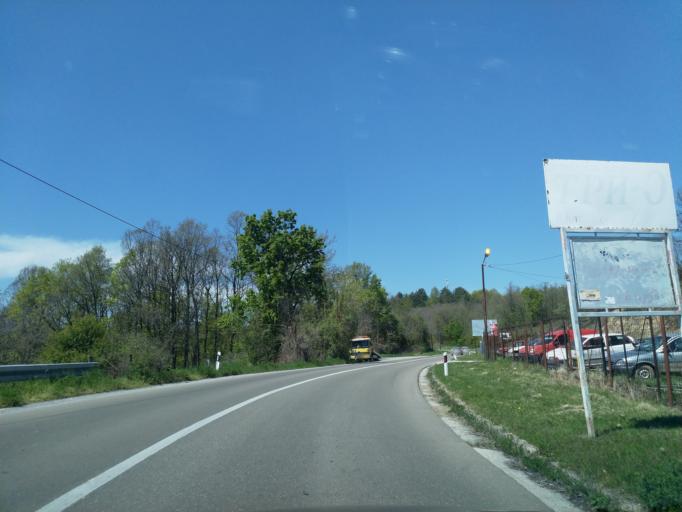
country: RS
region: Central Serbia
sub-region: Belgrade
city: Lazarevac
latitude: 44.3645
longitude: 20.3373
